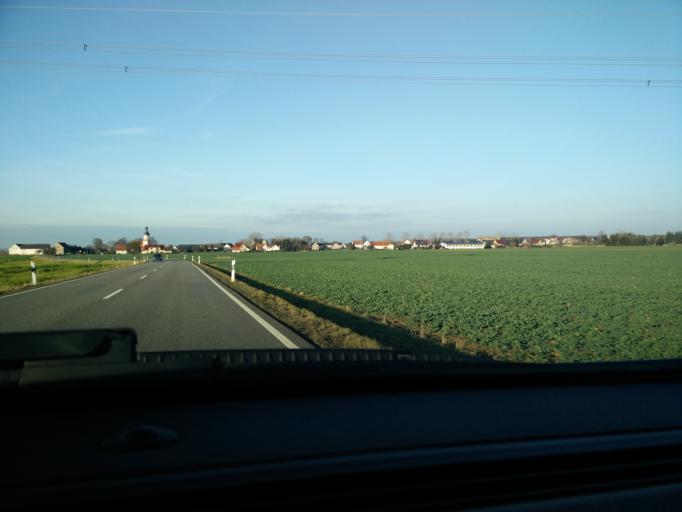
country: DE
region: Saxony
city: Geithain
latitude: 51.0949
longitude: 12.7024
